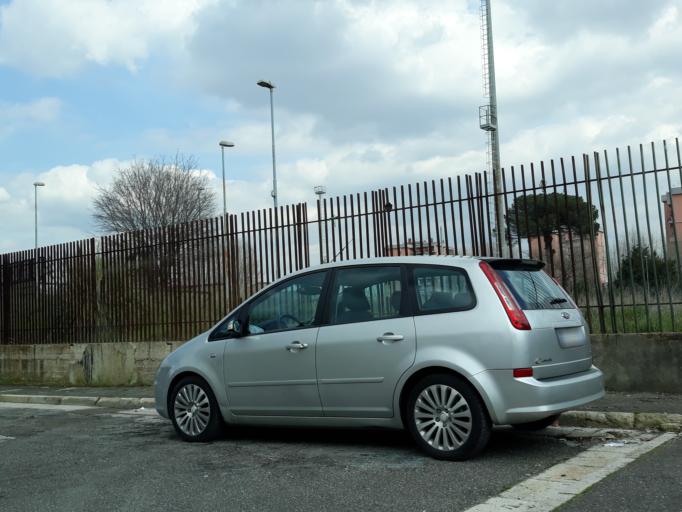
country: IT
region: Campania
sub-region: Provincia di Napoli
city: Melito di Napoli
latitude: 40.8894
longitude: 14.2332
